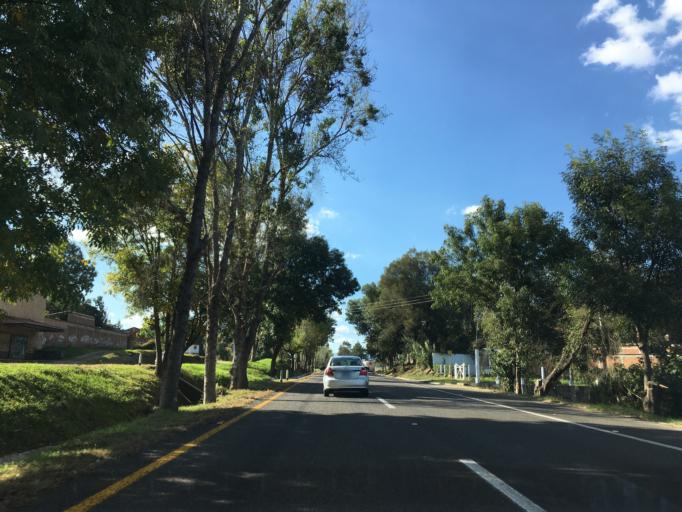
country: MX
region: Michoacan
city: Patzcuaro
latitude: 19.5328
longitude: -101.5663
